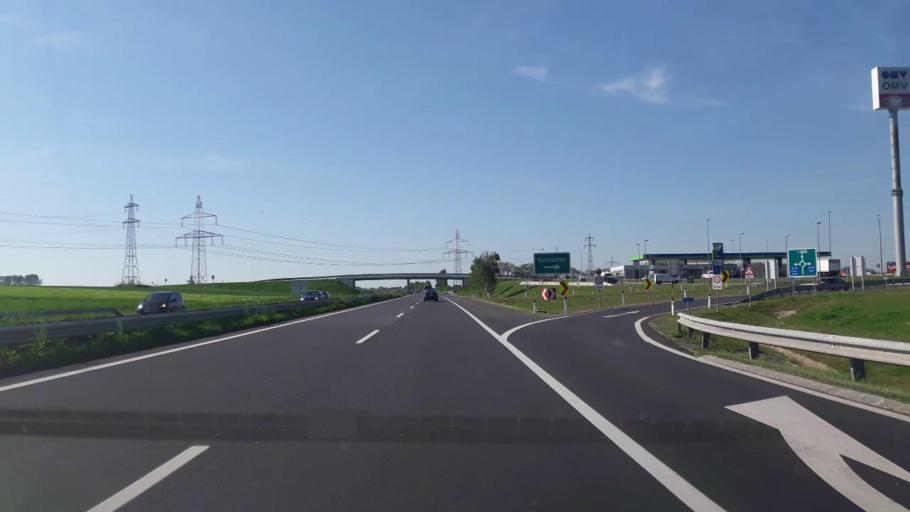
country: AT
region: Burgenland
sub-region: Eisenstadt-Umgebung
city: Hornstein
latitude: 47.8798
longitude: 16.4155
